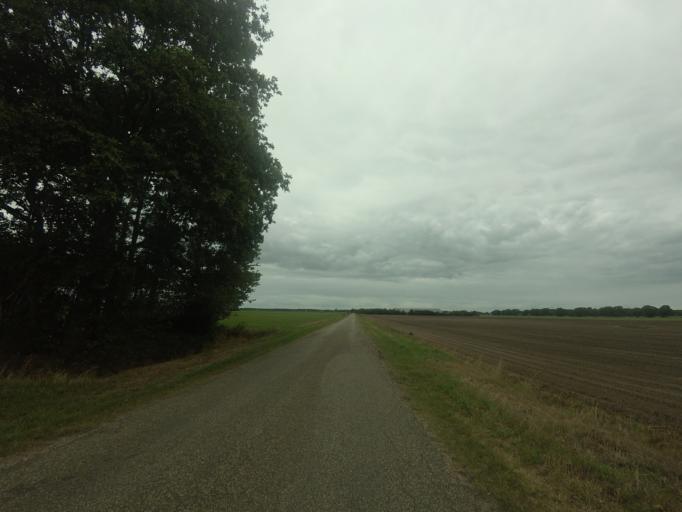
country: NL
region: Drenthe
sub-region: Gemeente Westerveld
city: Dwingeloo
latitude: 52.9580
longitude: 6.3155
